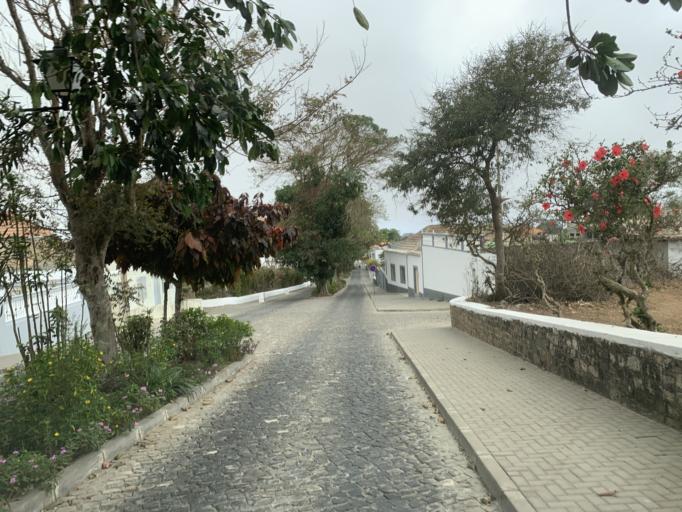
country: CV
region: Brava
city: Vila Nova Sintra
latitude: 14.8703
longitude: -24.6984
